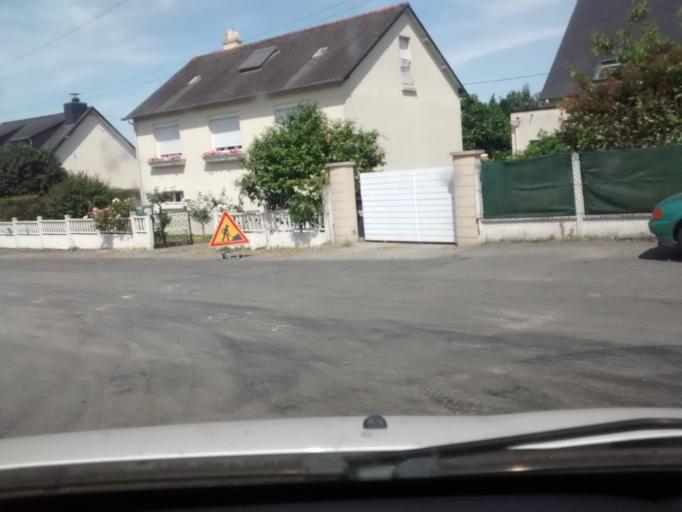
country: FR
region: Brittany
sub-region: Departement d'Ille-et-Vilaine
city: Cesson-Sevigne
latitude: 48.1036
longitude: -1.6040
